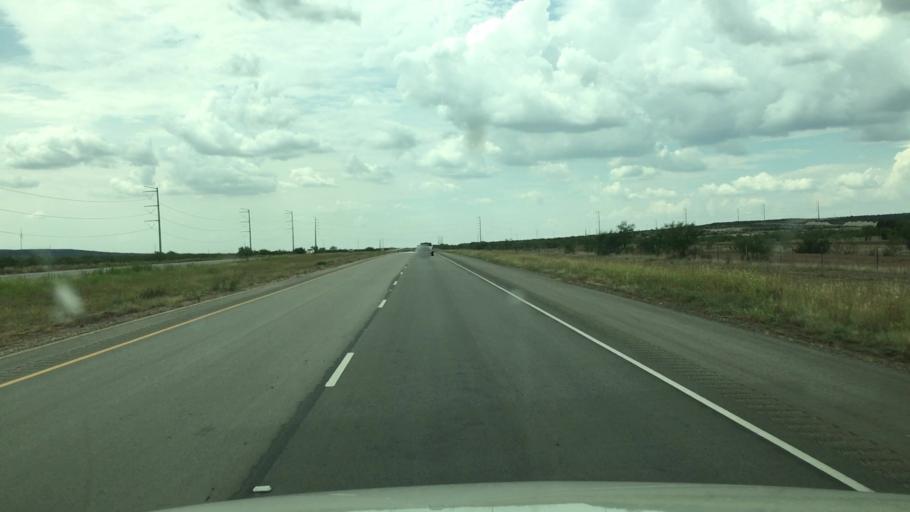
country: US
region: Texas
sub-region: Glasscock County
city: Garden City
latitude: 31.9806
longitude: -101.2547
